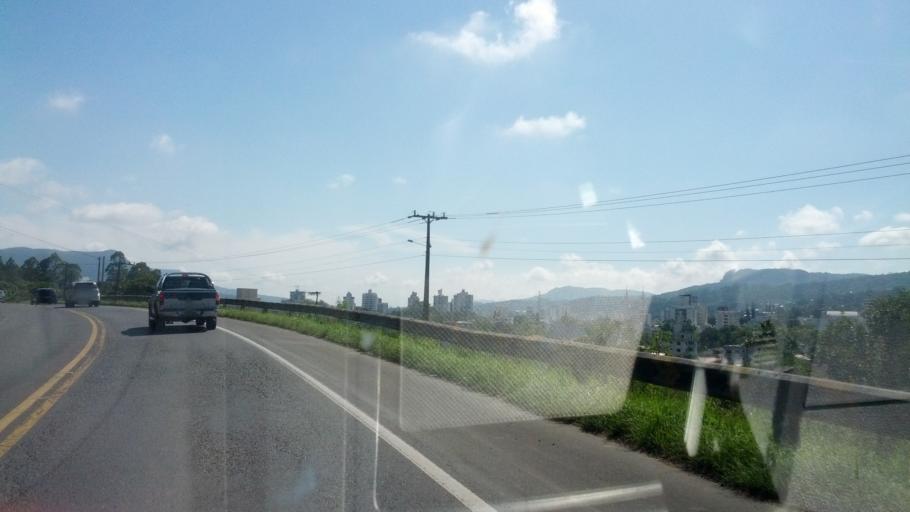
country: BR
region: Santa Catarina
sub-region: Rio Do Sul
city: Rio do Sul
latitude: -27.2178
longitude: -49.6550
